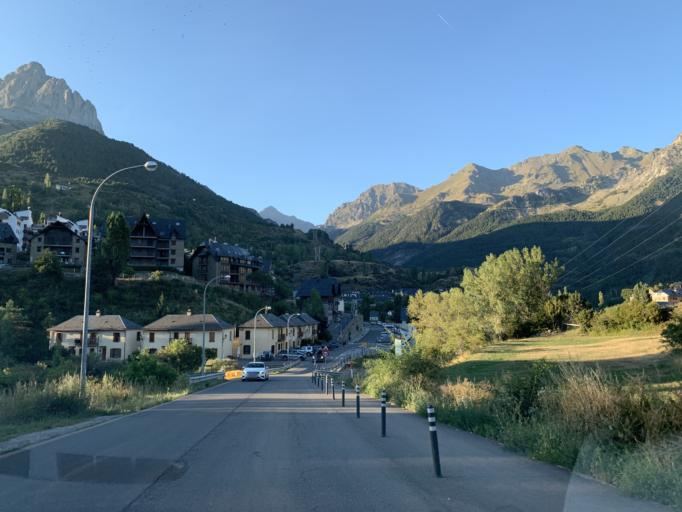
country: ES
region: Aragon
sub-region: Provincia de Huesca
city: Sallent de Gallego
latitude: 42.7679
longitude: -0.3351
